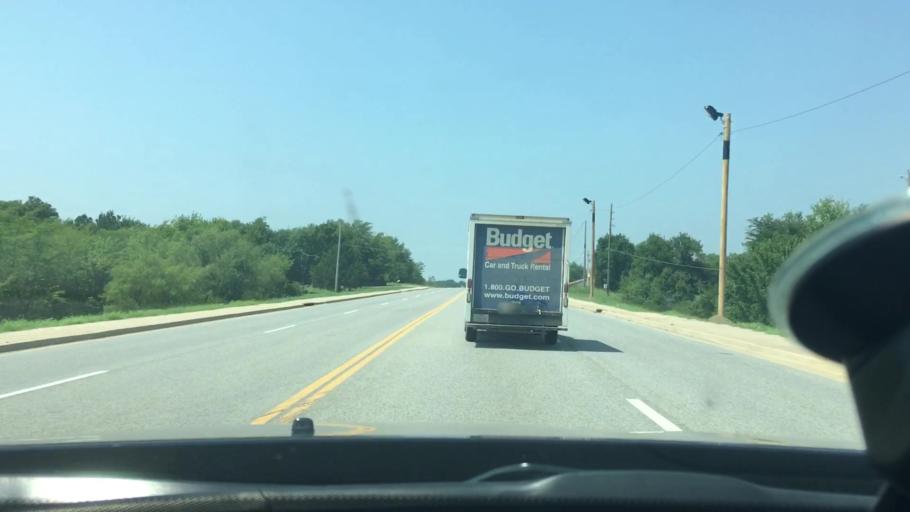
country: US
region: Oklahoma
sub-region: Atoka County
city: Atoka
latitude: 34.3748
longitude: -96.1236
